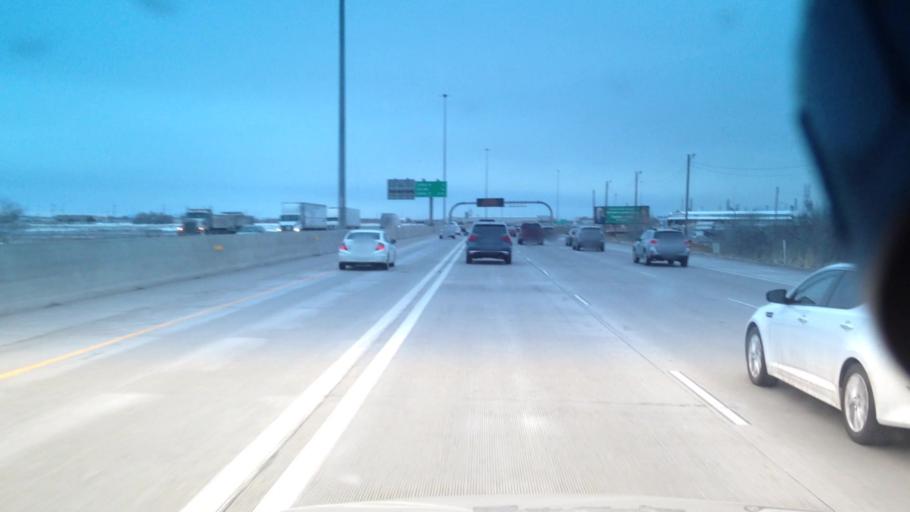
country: US
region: Utah
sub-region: Davis County
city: North Salt Lake
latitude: 40.8051
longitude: -111.9224
